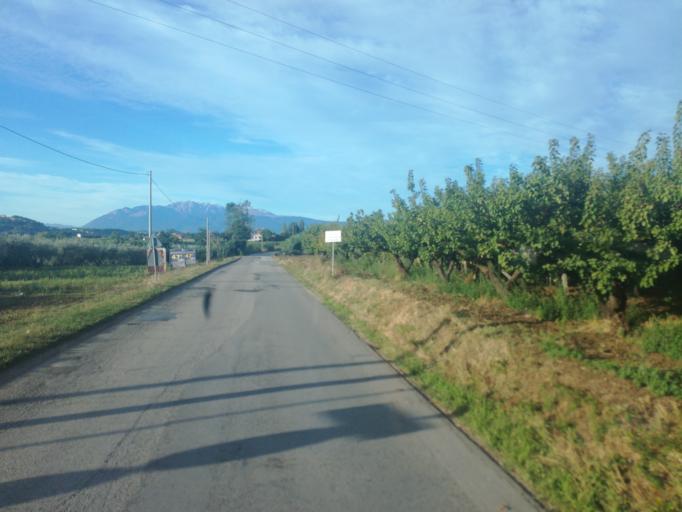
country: IT
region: Abruzzo
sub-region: Provincia di Chieti
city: Miglianico
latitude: 42.3868
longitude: 14.2950
